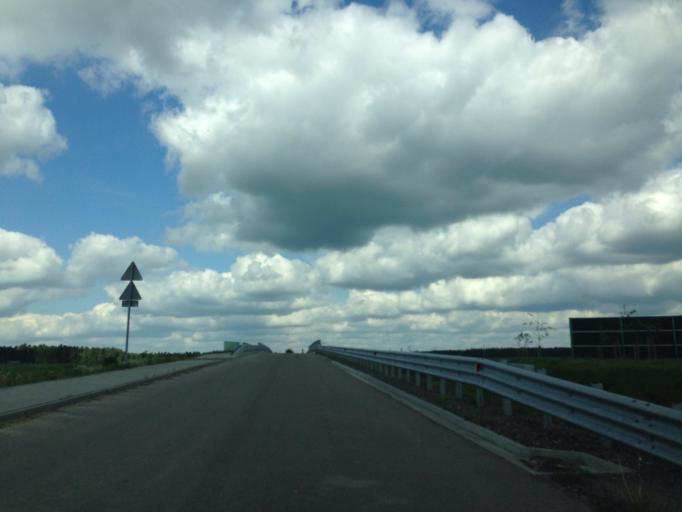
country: PL
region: Warmian-Masurian Voivodeship
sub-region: Powiat nidzicki
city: Nidzica
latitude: 53.4420
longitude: 20.3353
